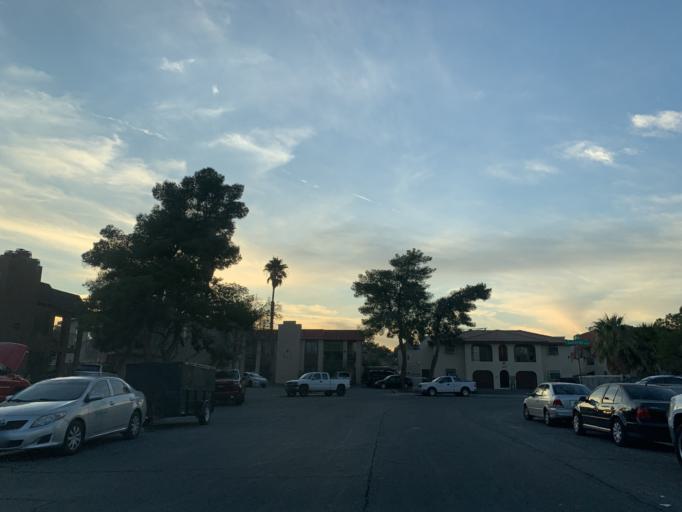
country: US
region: Nevada
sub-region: Clark County
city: Spring Valley
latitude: 36.1125
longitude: -115.2141
